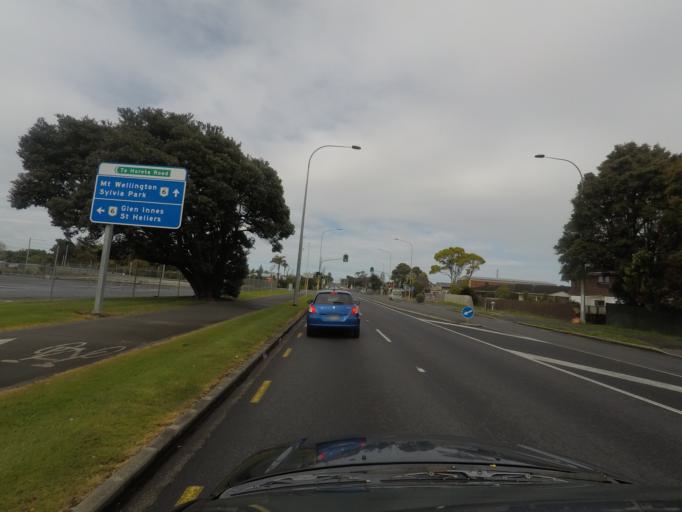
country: NZ
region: Auckland
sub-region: Auckland
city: Tamaki
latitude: -36.9027
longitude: 174.8424
